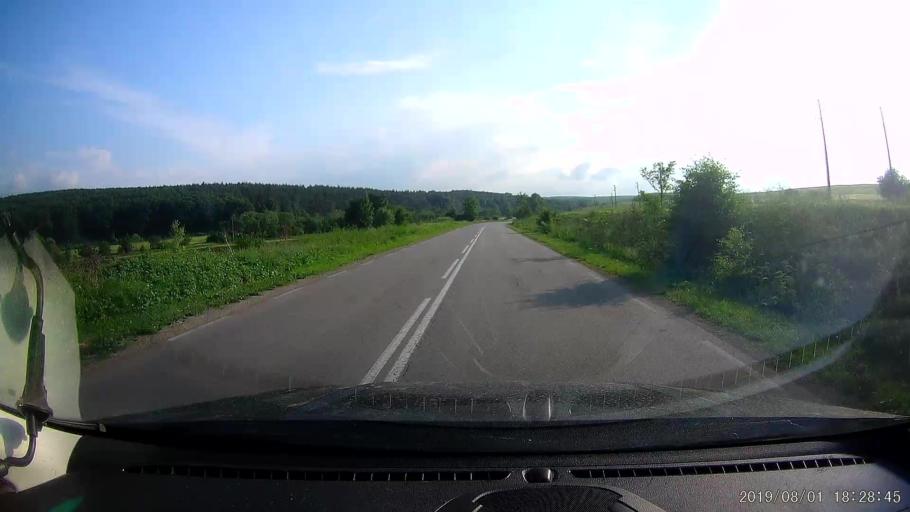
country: BG
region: Shumen
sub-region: Obshtina Venets
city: Venets
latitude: 43.5706
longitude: 26.9575
